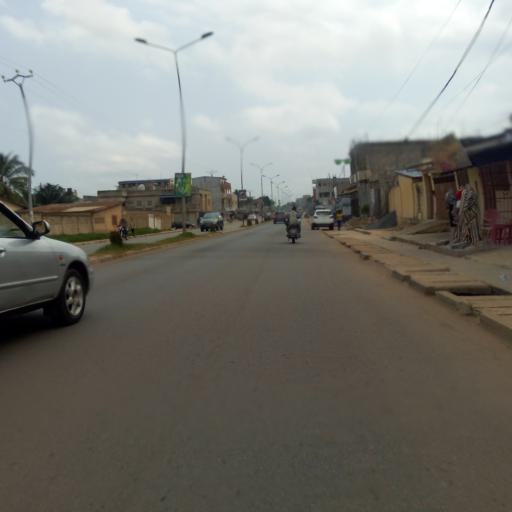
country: TG
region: Maritime
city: Lome
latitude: 6.1947
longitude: 1.1747
